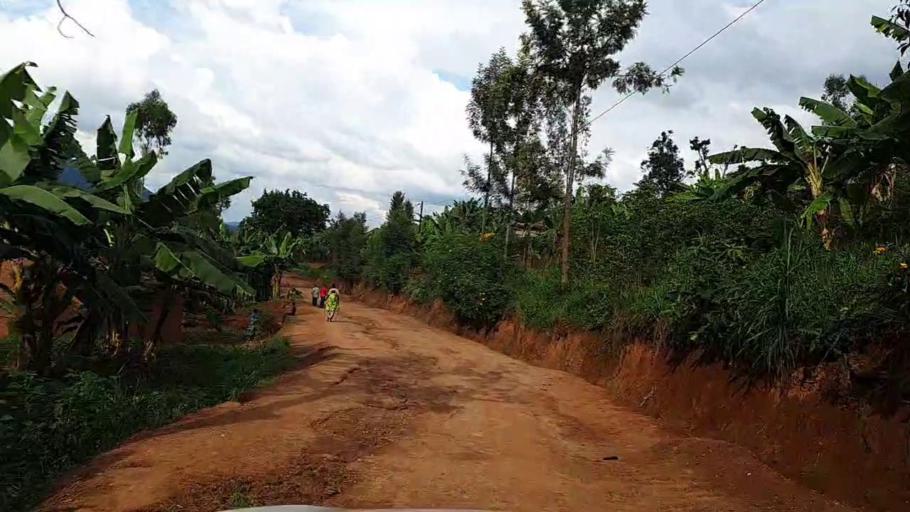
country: RW
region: Southern Province
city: Gikongoro
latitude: -2.4241
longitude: 29.6464
